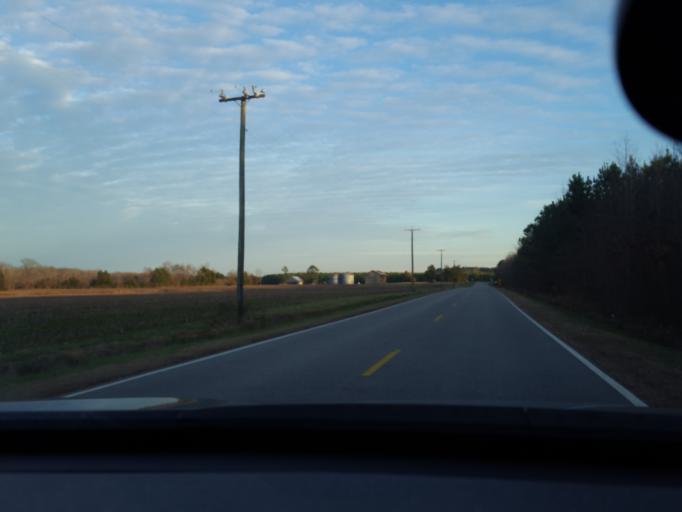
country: US
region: North Carolina
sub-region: Hertford County
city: Murfreesboro
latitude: 36.2782
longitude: -77.1599
